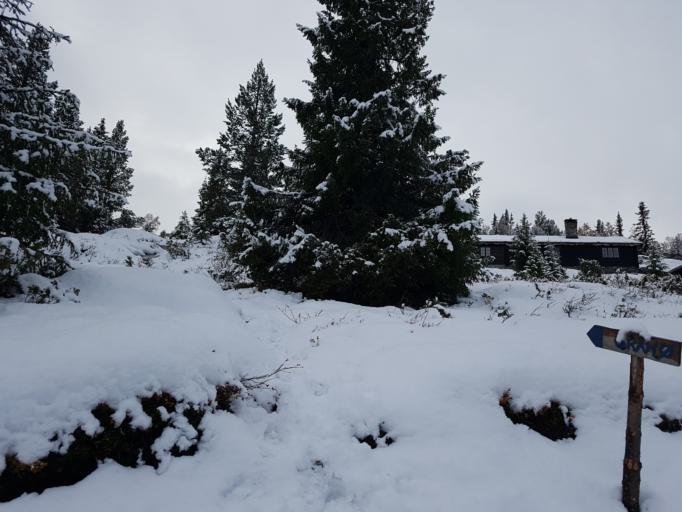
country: NO
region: Oppland
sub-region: Sel
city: Otta
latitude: 61.8068
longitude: 9.6777
